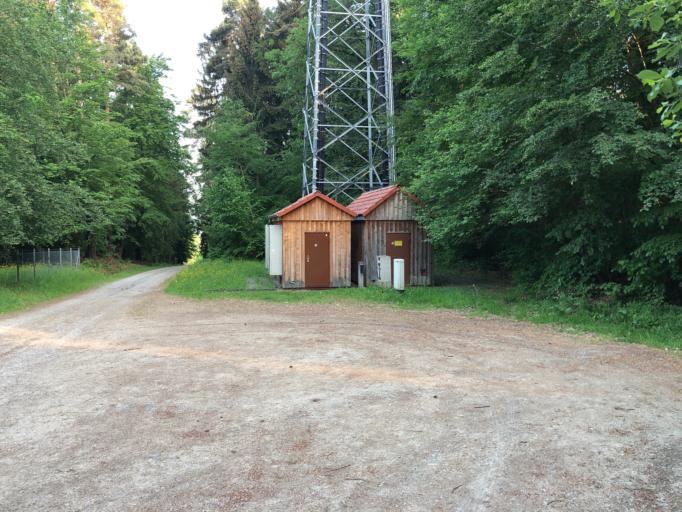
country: DE
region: Baden-Wuerttemberg
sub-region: Tuebingen Region
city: Tuebingen
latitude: 48.5440
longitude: 9.0381
